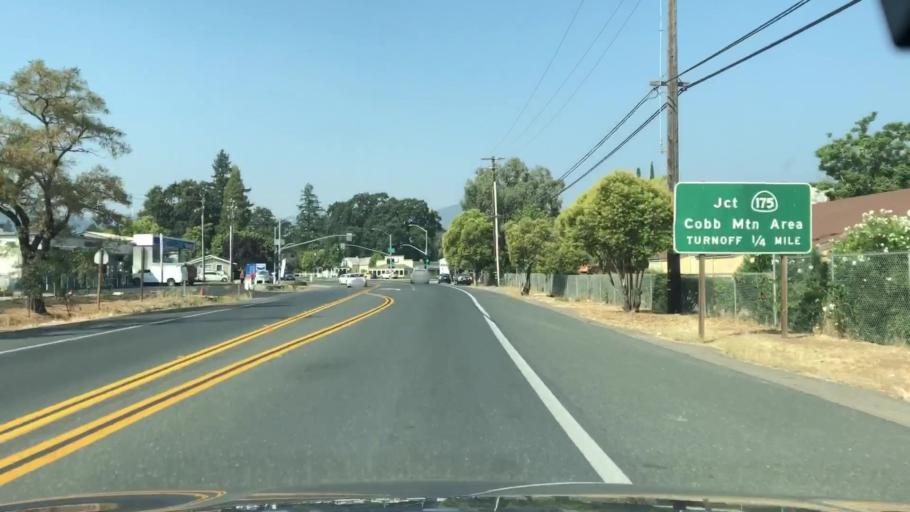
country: US
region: California
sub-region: Lake County
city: Middletown
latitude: 38.7549
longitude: -122.6125
